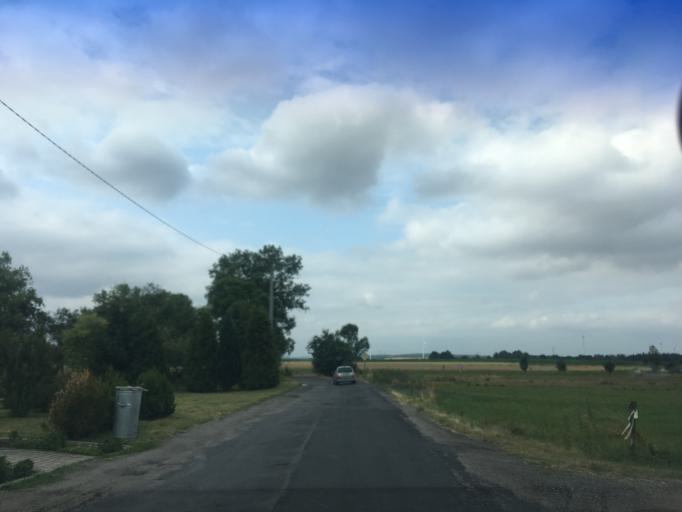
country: PL
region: Lower Silesian Voivodeship
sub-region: Powiat zgorzelecki
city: Sulikow
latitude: 51.1016
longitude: 15.0655
